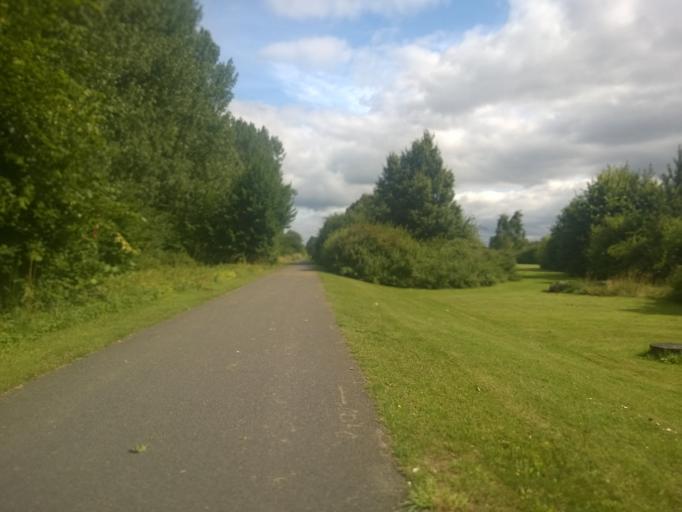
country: SE
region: Skane
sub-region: Kristianstads Kommun
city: Kristianstad
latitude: 56.0490
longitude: 14.1667
